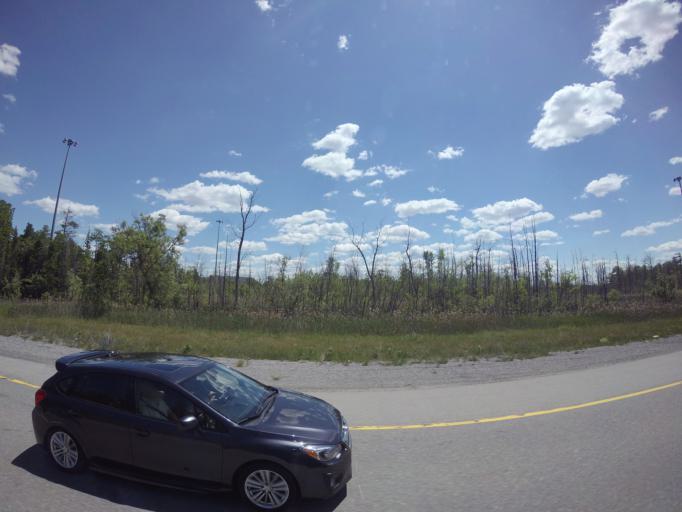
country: CA
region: Ontario
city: Bells Corners
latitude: 45.2756
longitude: -75.9688
